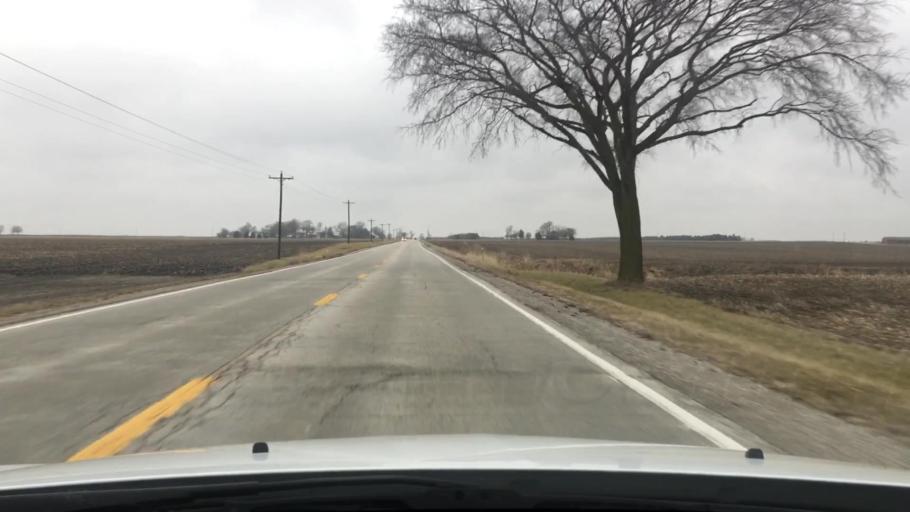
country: US
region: Illinois
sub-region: Iroquois County
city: Clifton
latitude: 40.8874
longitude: -87.8556
